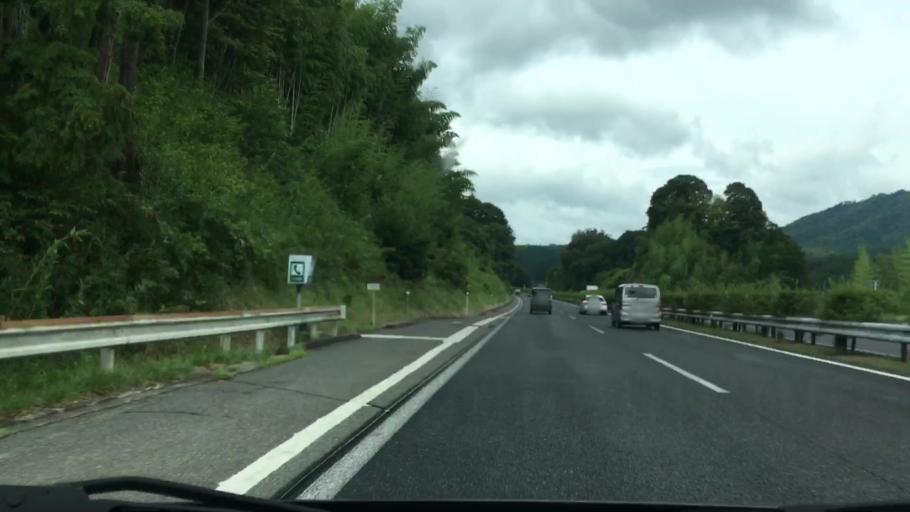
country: JP
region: Okayama
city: Tsuyama
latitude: 35.0622
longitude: 133.8567
